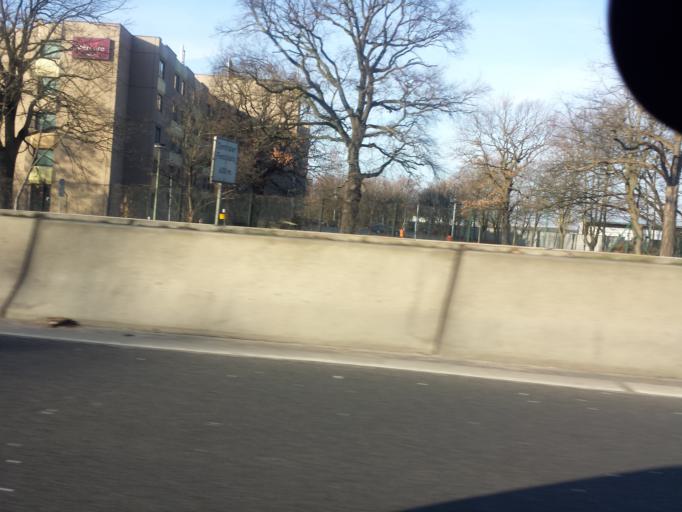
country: DE
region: Berlin
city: Charlottenburg-Nord
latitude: 52.5518
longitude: 13.3039
